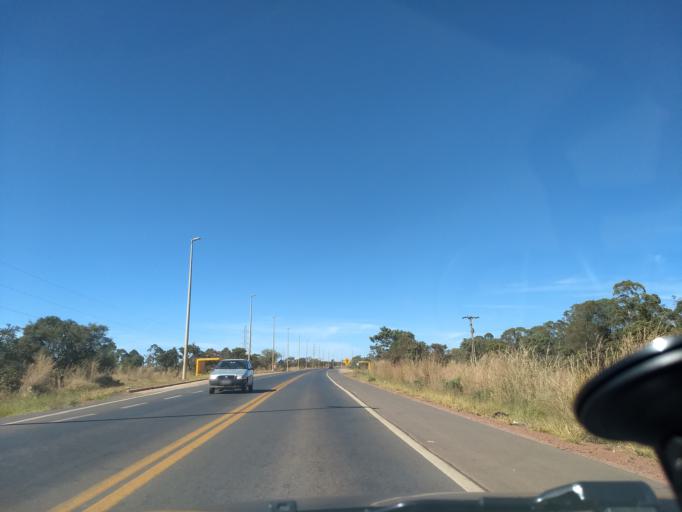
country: BR
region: Federal District
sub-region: Brasilia
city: Brasilia
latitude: -15.7588
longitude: -48.0458
